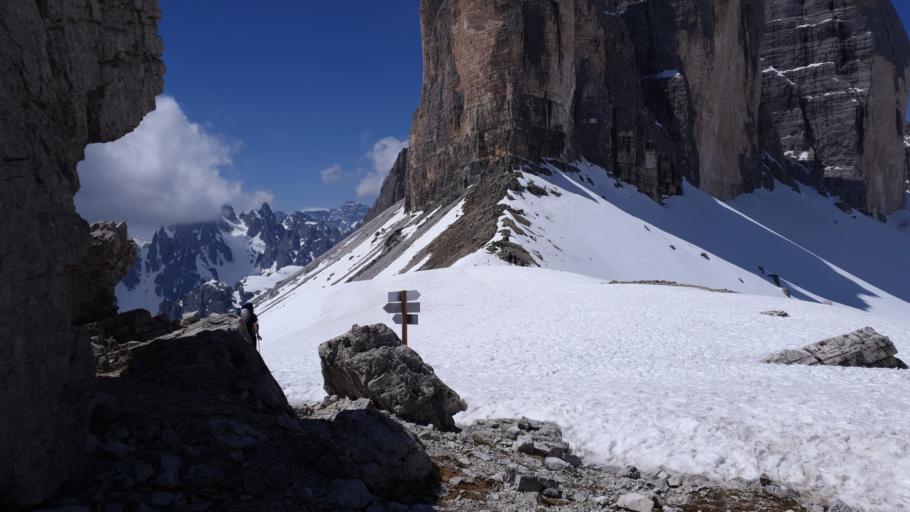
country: IT
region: Trentino-Alto Adige
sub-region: Bolzano
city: Sesto
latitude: 46.6234
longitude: 12.3127
